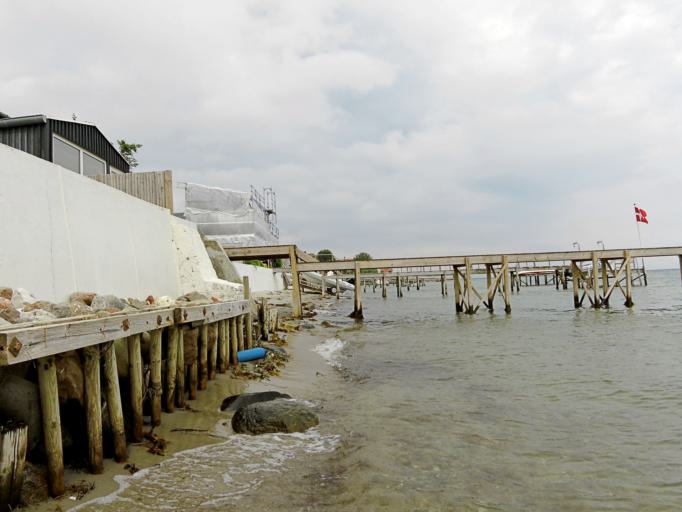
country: DK
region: Capital Region
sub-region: Gentofte Kommune
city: Charlottenlund
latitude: 55.7834
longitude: 12.5939
